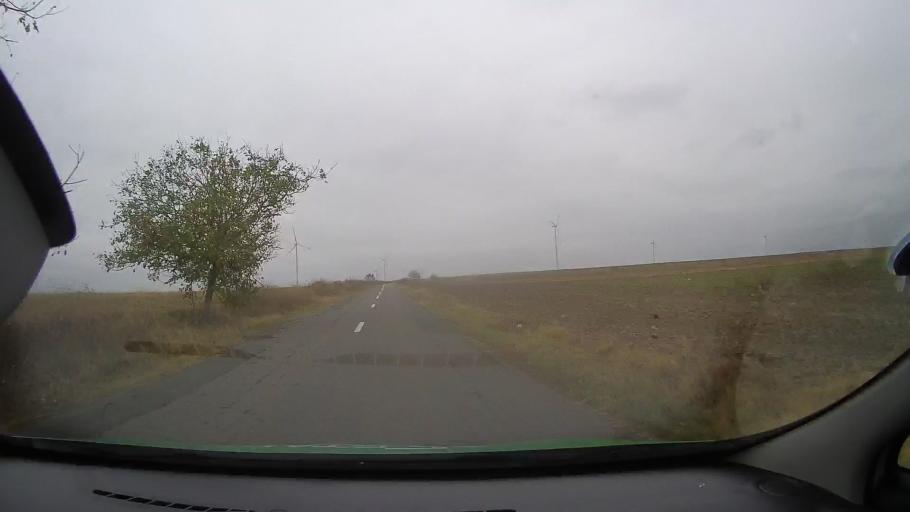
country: RO
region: Constanta
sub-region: Comuna Pantelimon
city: Pantelimon
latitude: 44.5013
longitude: 28.3541
